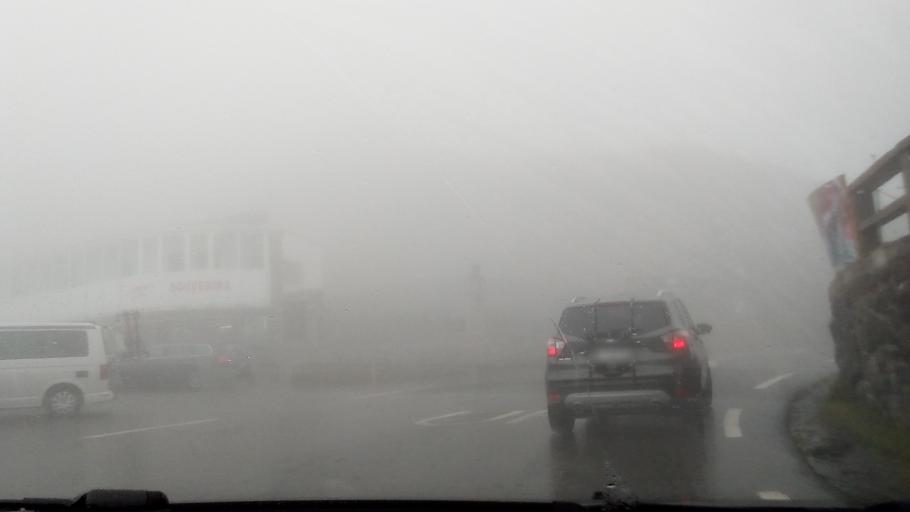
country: FR
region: Midi-Pyrenees
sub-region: Departement des Hautes-Pyrenees
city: Campan
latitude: 42.9081
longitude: 0.1452
